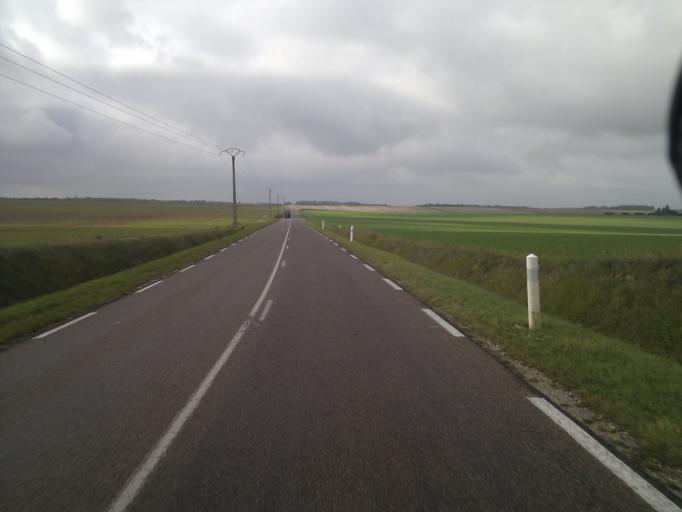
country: FR
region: Champagne-Ardenne
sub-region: Departement de la Haute-Marne
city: Chaumont
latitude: 48.1511
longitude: 5.2089
